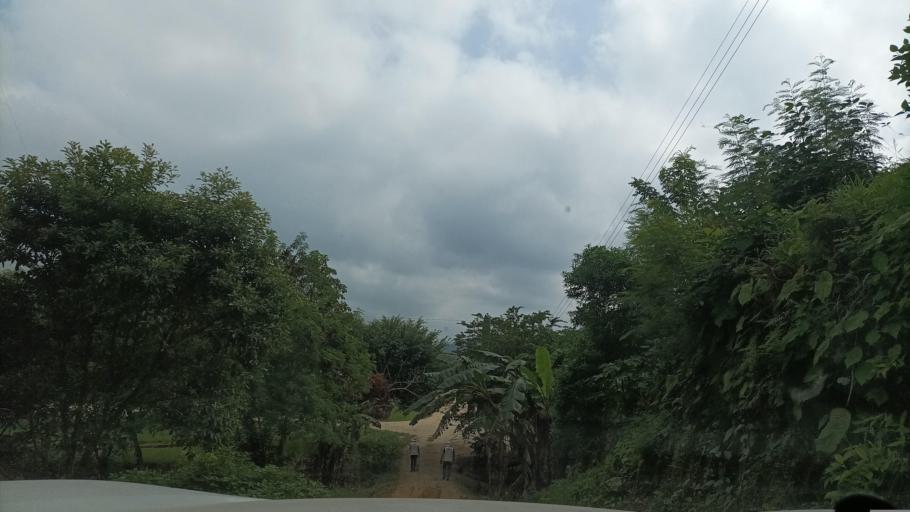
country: MX
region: Veracruz
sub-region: Uxpanapa
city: Poblado Cinco
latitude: 17.4618
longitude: -94.6053
